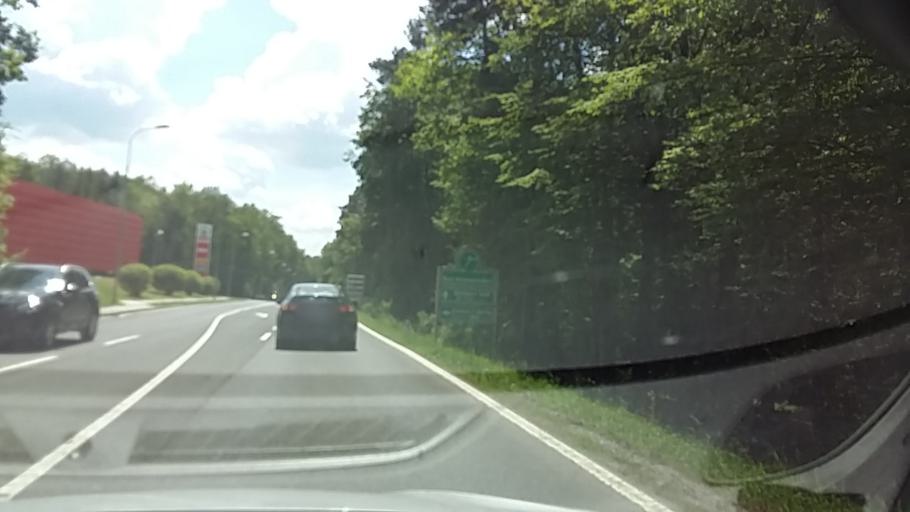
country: AT
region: Burgenland
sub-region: Politischer Bezirk Oberwart
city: Bad Tatzmannsdorf
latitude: 47.3362
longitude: 16.2198
